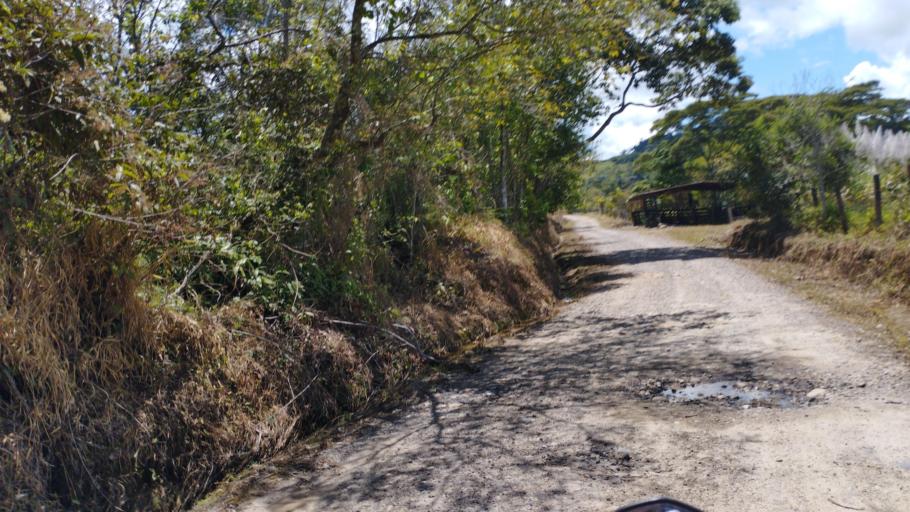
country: CO
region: Boyaca
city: San Luis de Gaceno
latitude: 4.7594
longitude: -73.1351
